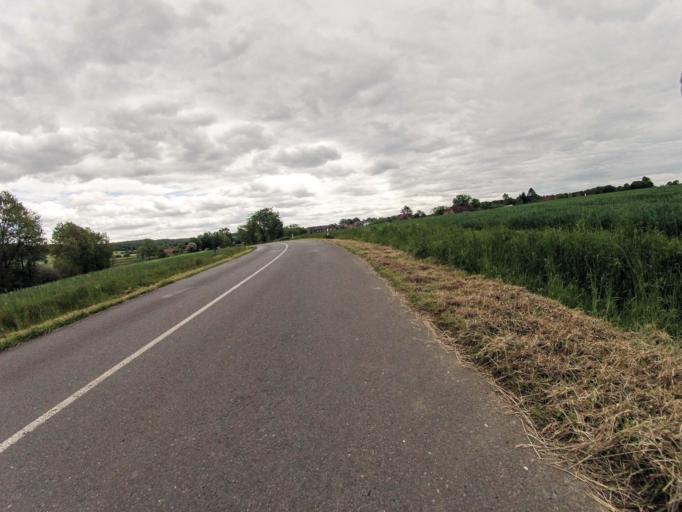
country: DE
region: Lower Saxony
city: Laar
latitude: 52.3342
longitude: 8.2534
